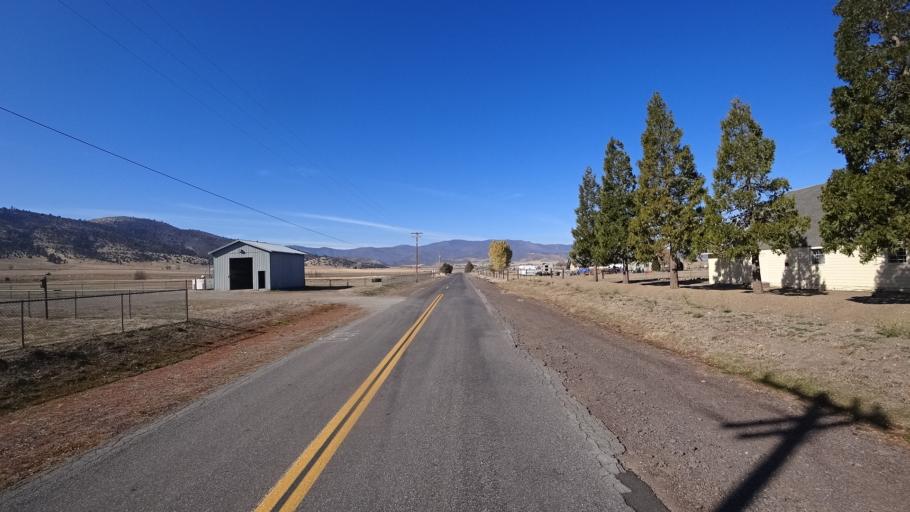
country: US
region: California
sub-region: Siskiyou County
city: Weed
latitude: 41.5208
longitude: -122.5234
